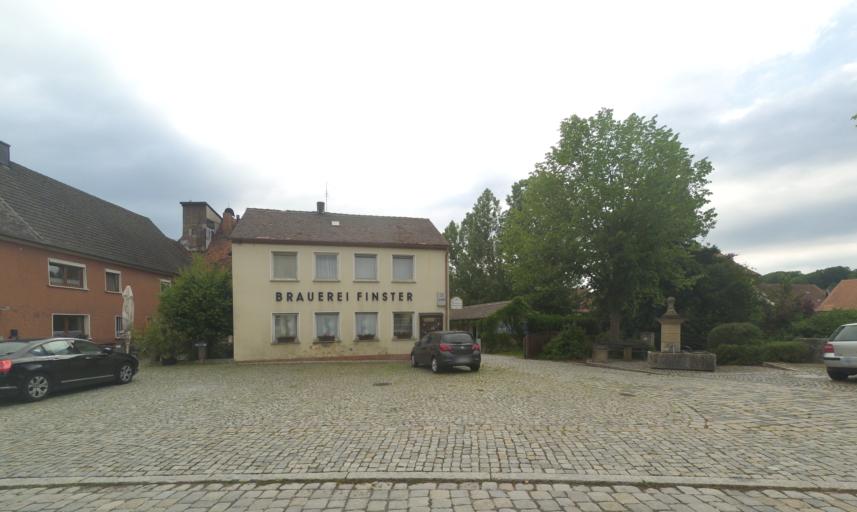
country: DE
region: Bavaria
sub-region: Regierungsbezirk Mittelfranken
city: Burghaslach
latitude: 49.7321
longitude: 10.5996
